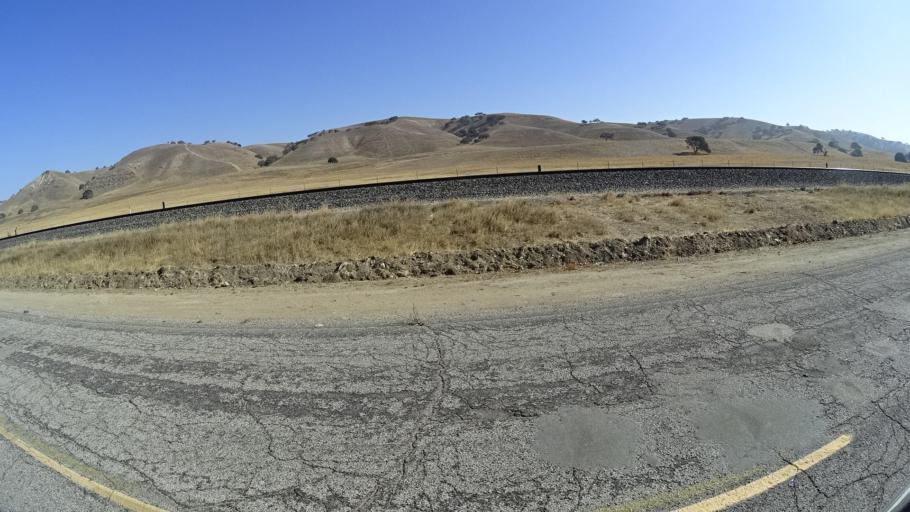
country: US
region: California
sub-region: San Luis Obispo County
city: San Miguel
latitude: 35.8532
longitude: -120.7595
